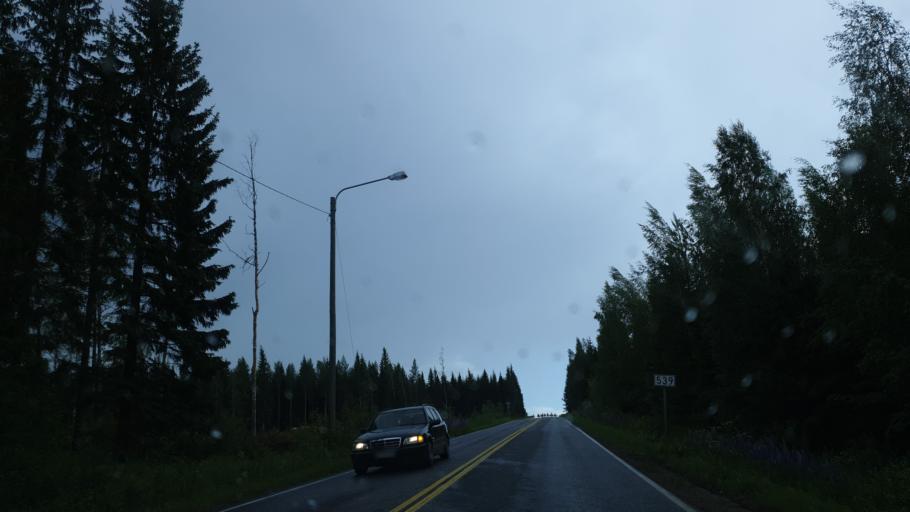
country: FI
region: Northern Savo
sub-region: Kuopio
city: Vehmersalmi
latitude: 62.9377
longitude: 27.9144
